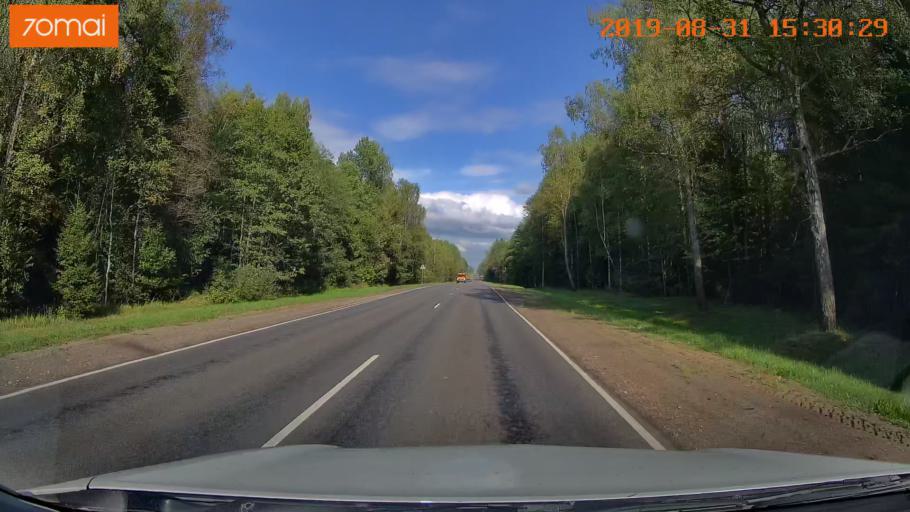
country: RU
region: Kaluga
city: Baryatino
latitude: 54.5760
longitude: 34.6312
